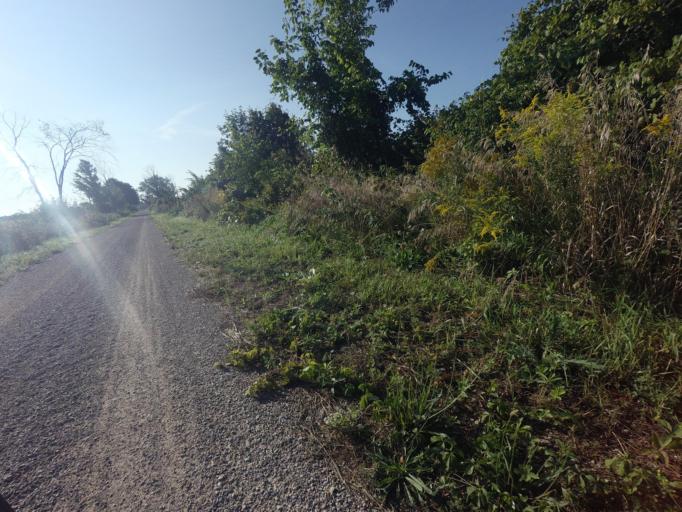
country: CA
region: Ontario
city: Goderich
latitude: 43.7548
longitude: -81.5113
